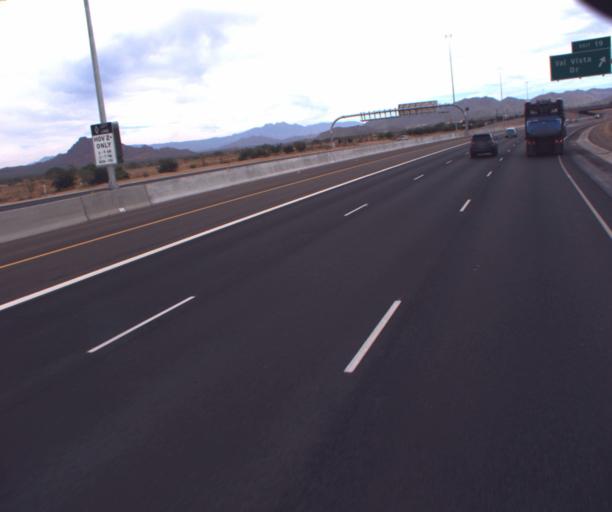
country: US
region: Arizona
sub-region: Maricopa County
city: Mesa
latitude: 33.4827
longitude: -111.7611
